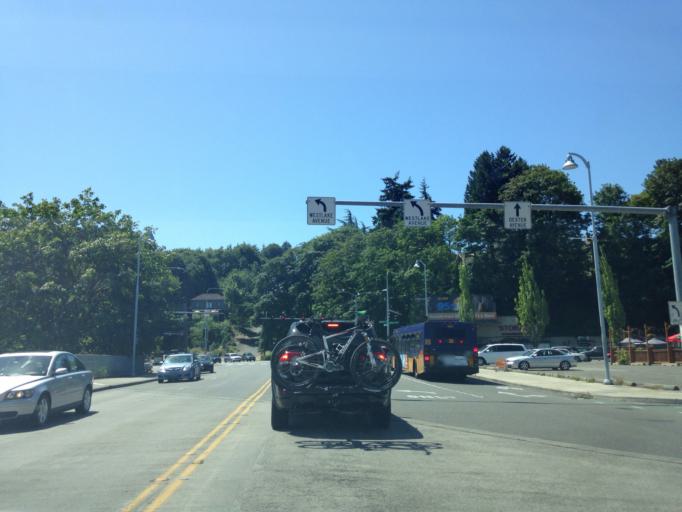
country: US
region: Washington
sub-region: King County
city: Seattle
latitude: 47.6470
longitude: -122.3498
